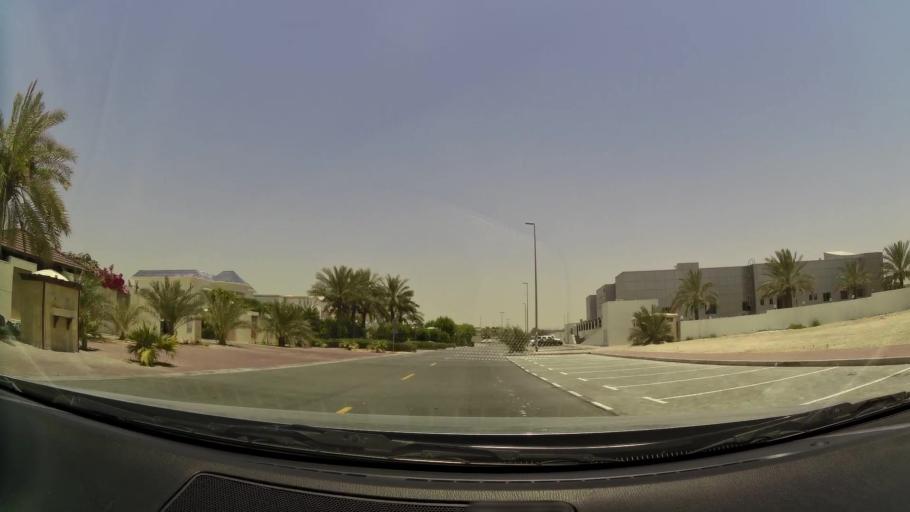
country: AE
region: Dubai
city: Dubai
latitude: 25.0924
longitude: 55.1875
